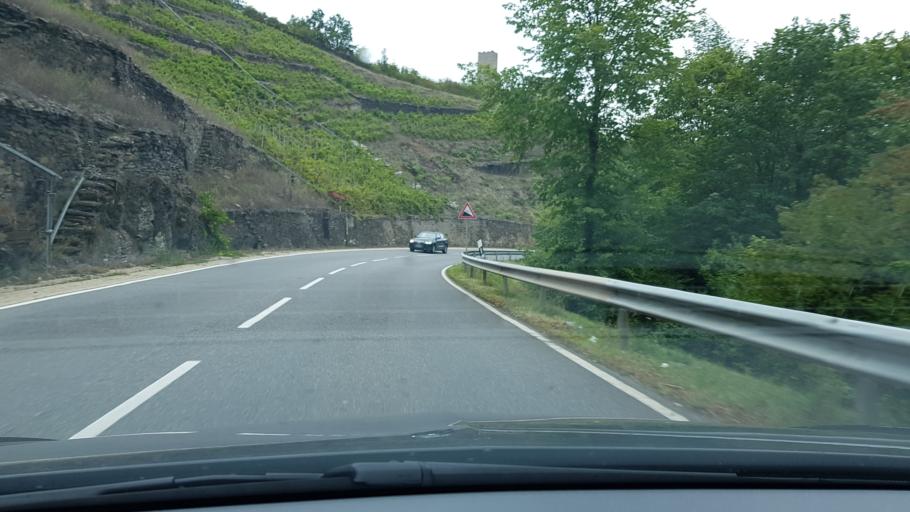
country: DE
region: Rheinland-Pfalz
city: Kobern-Gondorf
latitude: 50.3105
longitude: 7.4508
